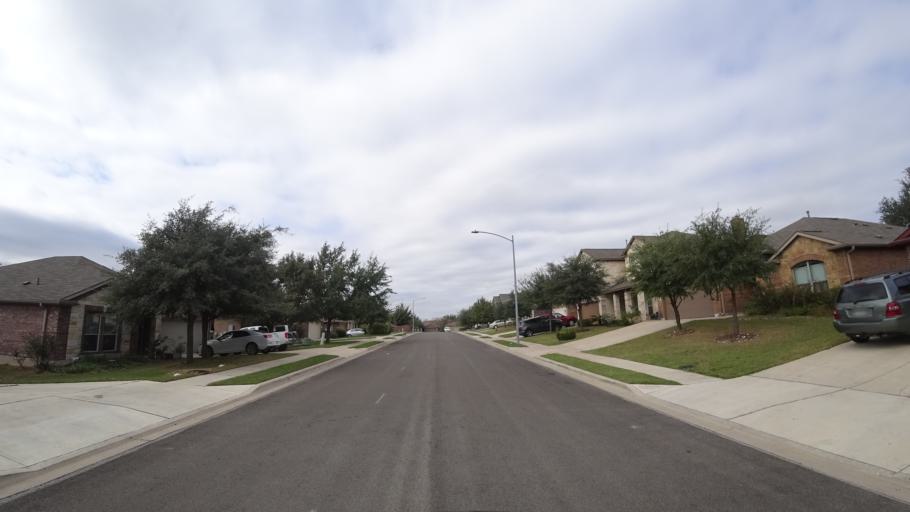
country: US
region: Texas
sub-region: Travis County
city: Manchaca
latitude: 30.1455
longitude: -97.8431
